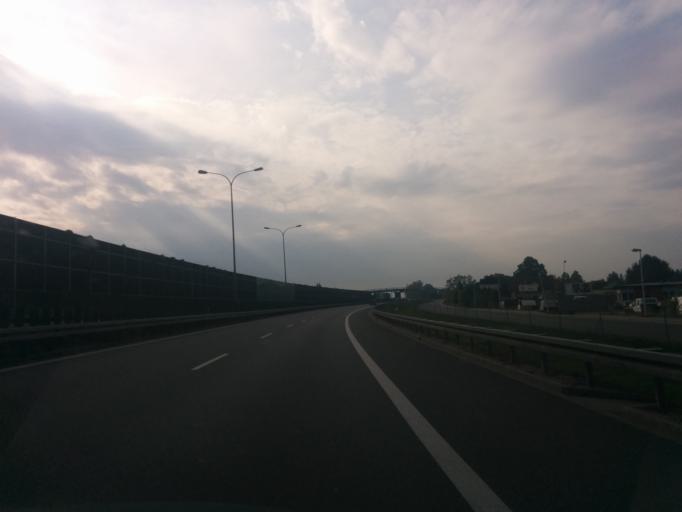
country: PL
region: Masovian Voivodeship
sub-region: Powiat bialobrzeski
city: Stara Blotnica
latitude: 51.5655
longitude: 21.0258
